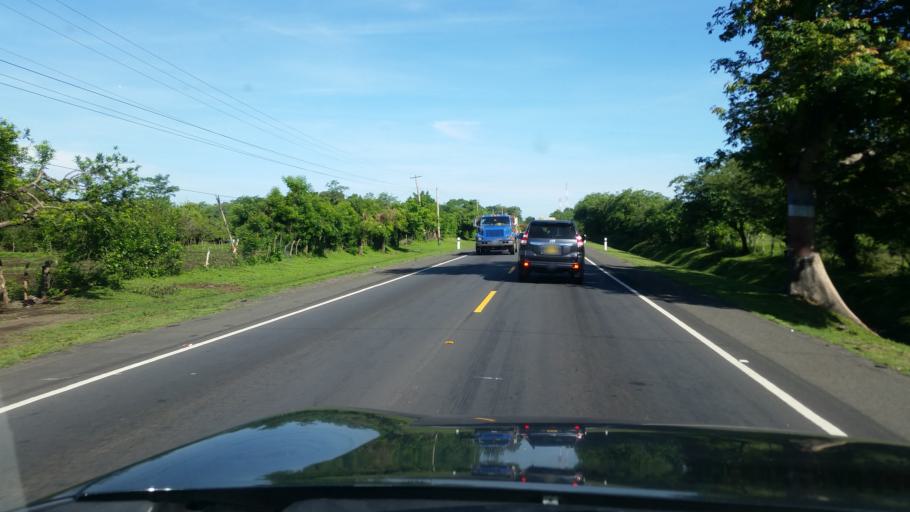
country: NI
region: Leon
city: Quezalguaque
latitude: 12.5486
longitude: -86.9302
